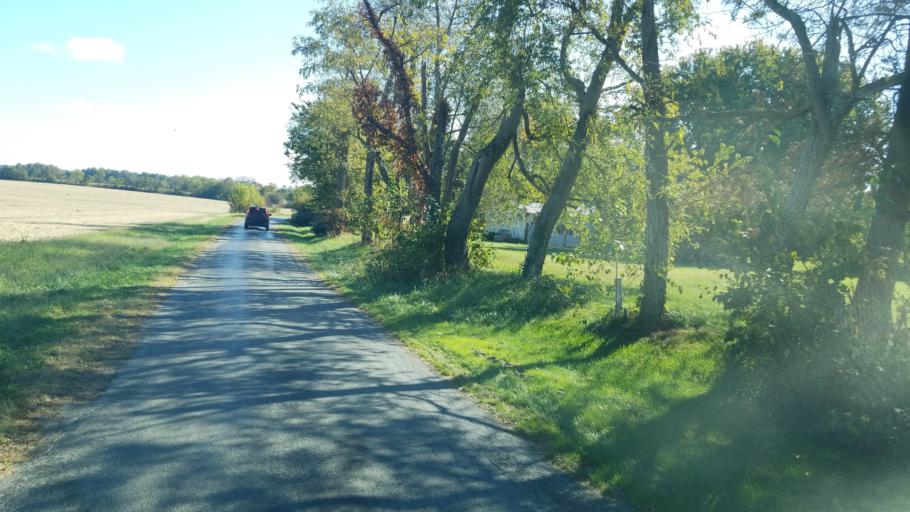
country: US
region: Ohio
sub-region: Highland County
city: Leesburg
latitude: 39.2870
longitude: -83.5811
